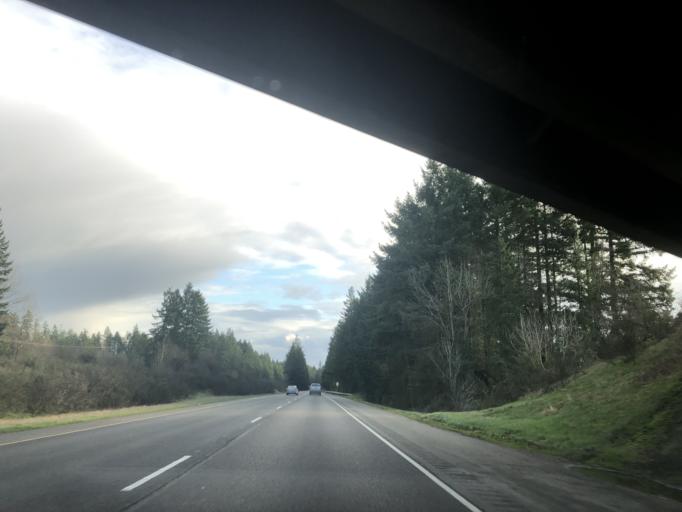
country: US
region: Washington
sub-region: Kitsap County
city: Bethel
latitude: 47.4847
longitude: -122.6311
